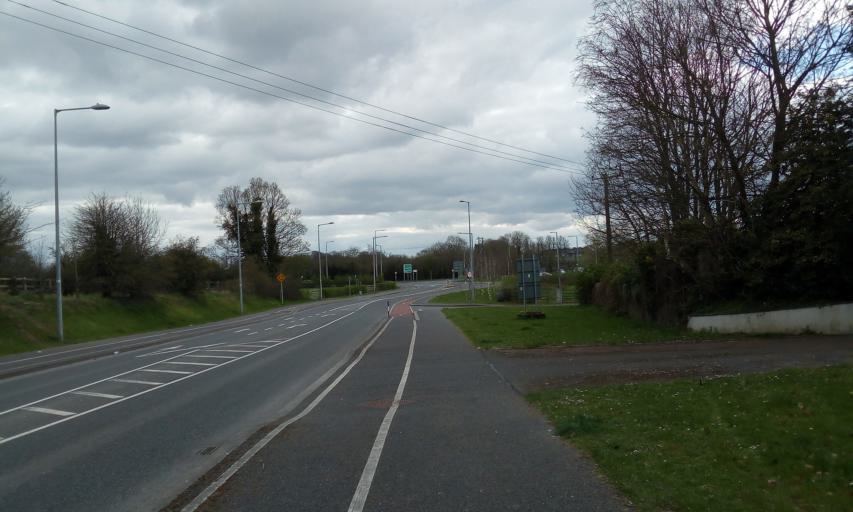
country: IE
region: Leinster
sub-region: Kilkenny
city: Kilkenny
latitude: 52.6393
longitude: -7.2570
